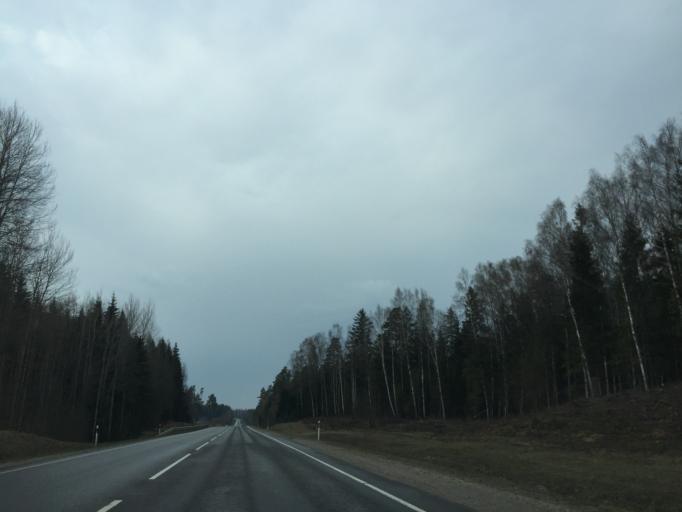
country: EE
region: Tartu
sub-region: UElenurme vald
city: Ulenurme
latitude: 58.1059
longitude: 26.7392
